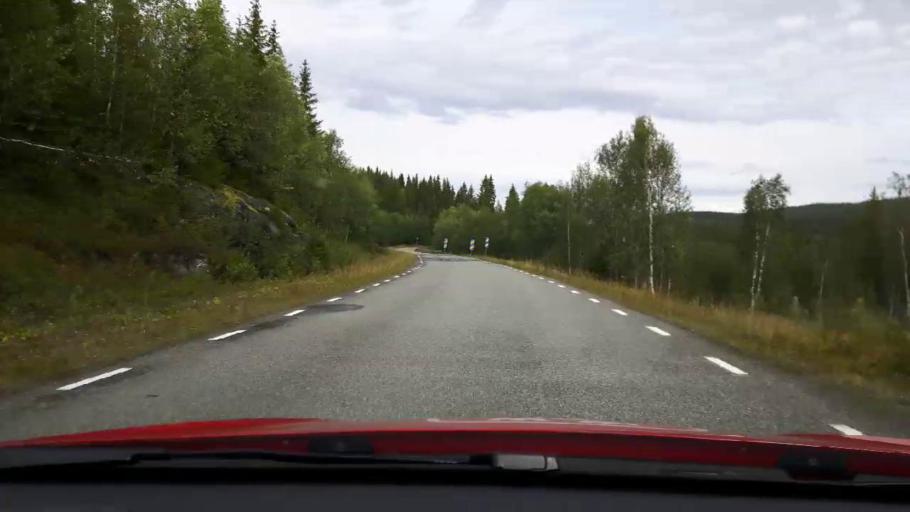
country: SE
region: Jaemtland
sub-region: Are Kommun
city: Are
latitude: 63.7426
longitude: 13.0797
